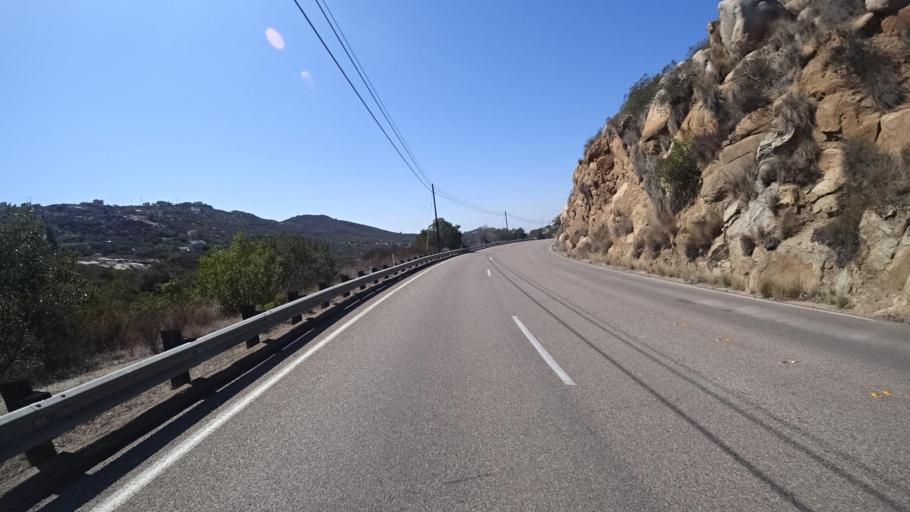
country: US
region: California
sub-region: San Diego County
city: Crest
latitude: 32.8123
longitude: -116.8738
